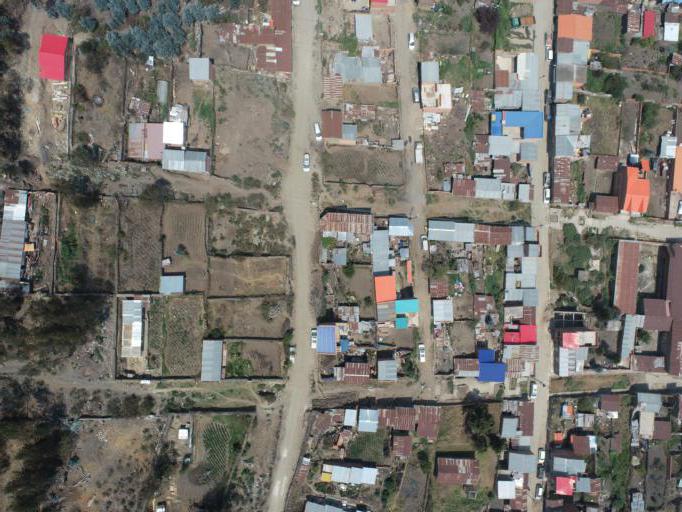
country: BO
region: La Paz
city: Quime
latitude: -16.9825
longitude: -67.2185
